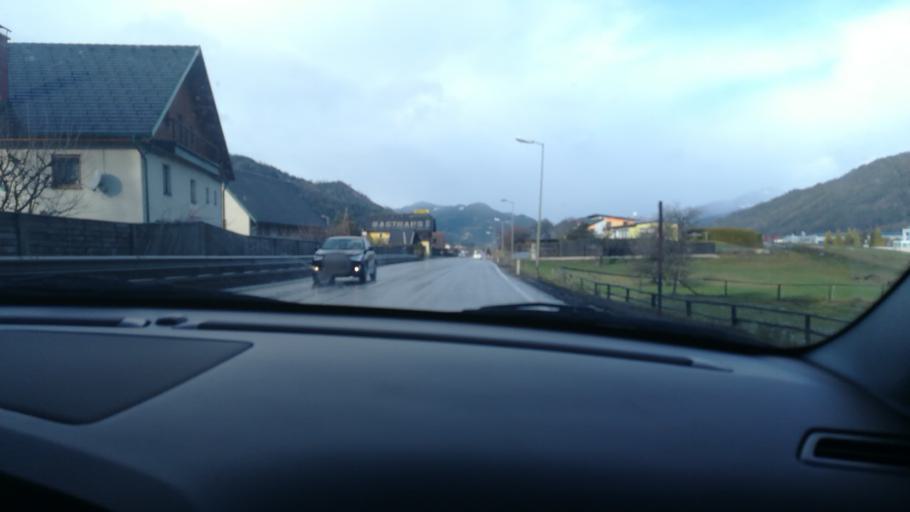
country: AT
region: Styria
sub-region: Politischer Bezirk Murtal
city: Sankt Peter ob Judenburg
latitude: 47.1761
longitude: 14.6087
